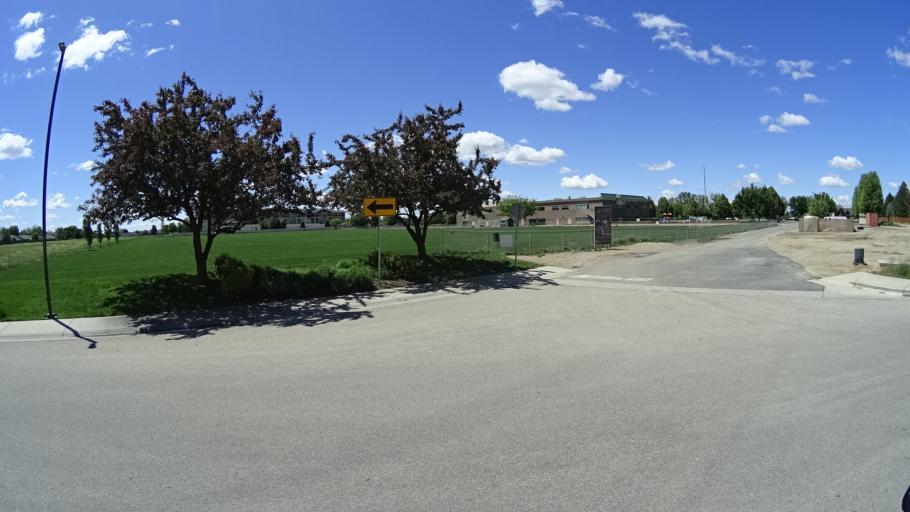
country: US
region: Idaho
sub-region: Ada County
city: Meridian
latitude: 43.6410
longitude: -116.3507
